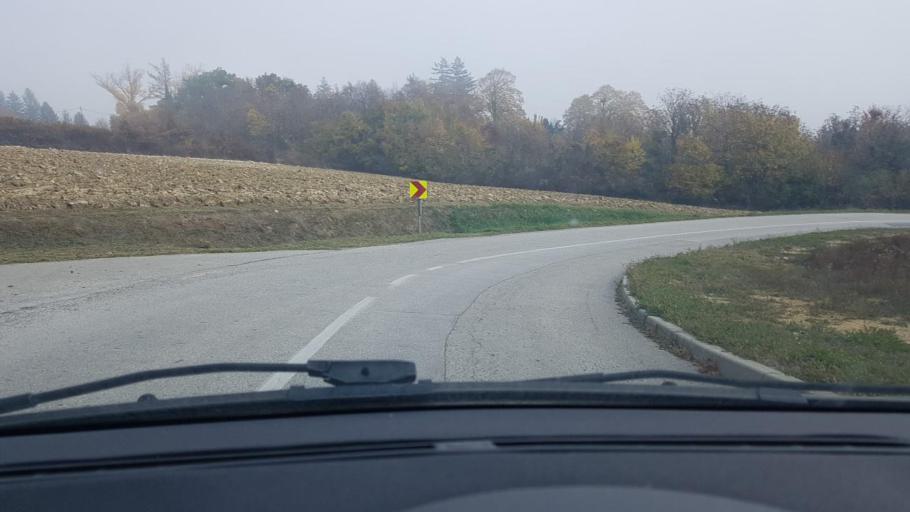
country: HR
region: Krapinsko-Zagorska
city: Zlatar
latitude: 46.1378
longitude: 16.1390
